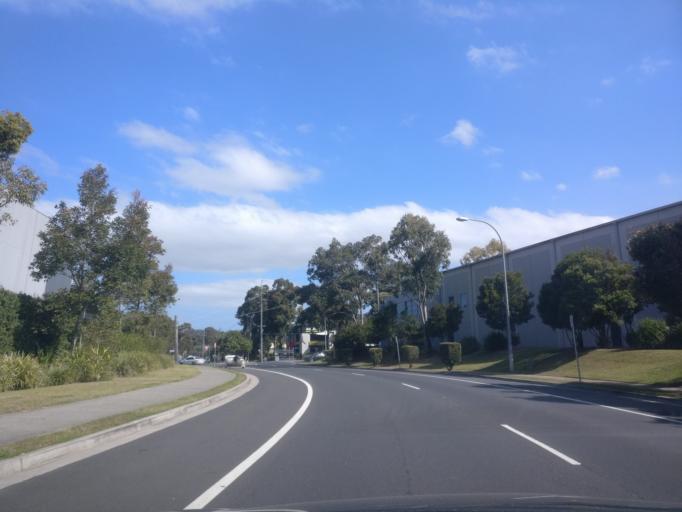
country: AU
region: New South Wales
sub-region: Pittwater
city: Warriewood
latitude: -33.6776
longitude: 151.2888
